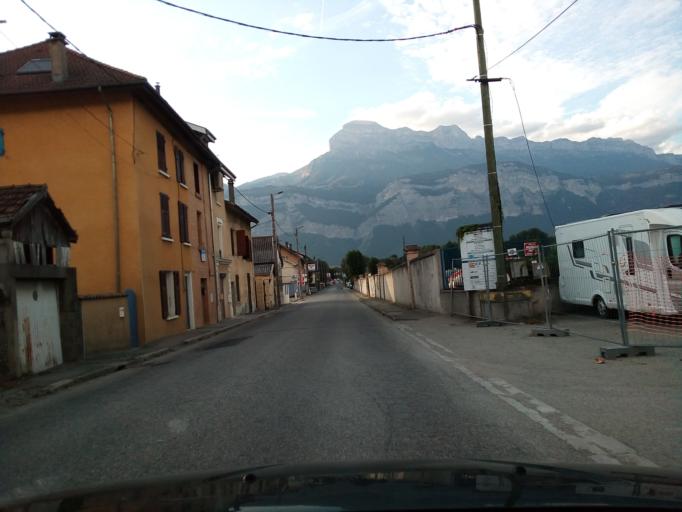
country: FR
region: Rhone-Alpes
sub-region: Departement de l'Isere
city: Froges
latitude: 45.2602
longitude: 5.9050
